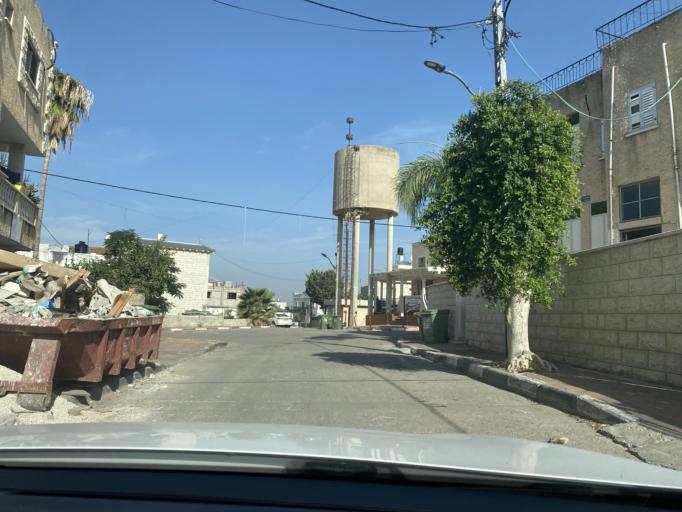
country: IL
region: Central District
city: Kafr Qasim
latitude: 32.1300
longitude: 34.9730
